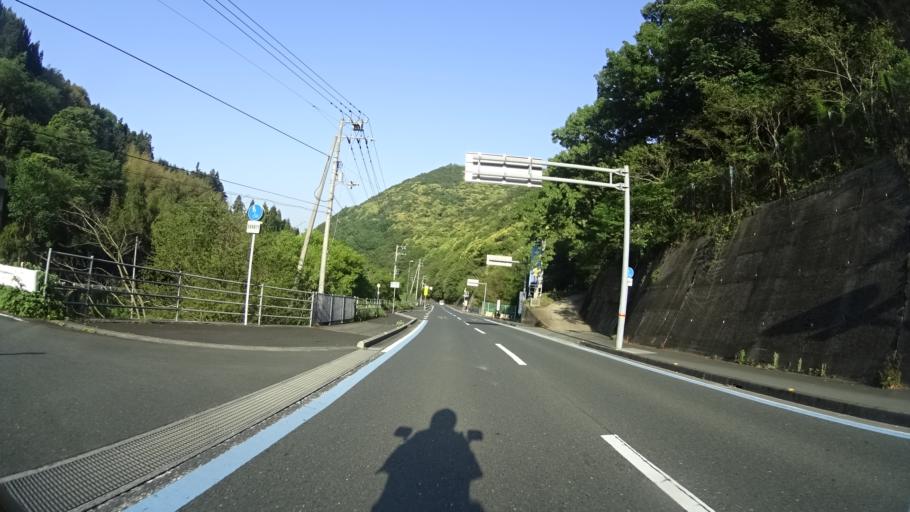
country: JP
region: Ehime
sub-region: Nishiuwa-gun
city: Ikata-cho
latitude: 33.4978
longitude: 132.3719
